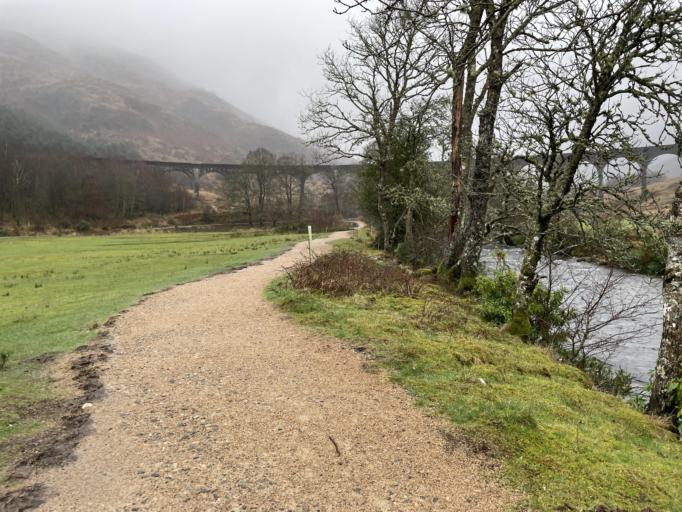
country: GB
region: Scotland
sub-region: Highland
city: Fort William
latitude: 56.8739
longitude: -5.4319
